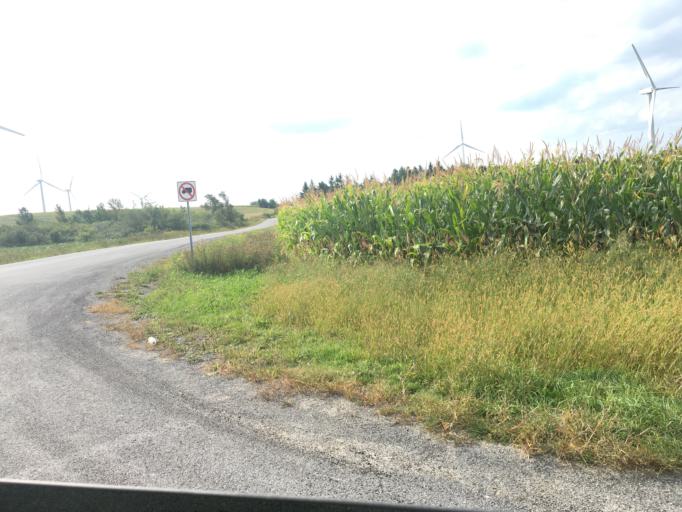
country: US
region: New York
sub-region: Madison County
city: Canastota
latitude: 42.9842
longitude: -75.7644
